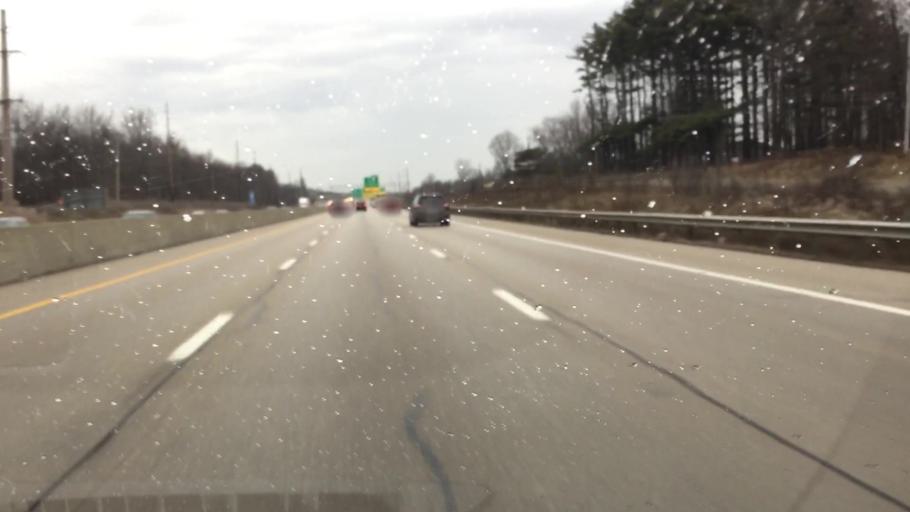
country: US
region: Ohio
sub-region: Summit County
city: Boston Heights
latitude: 41.2434
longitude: -81.4960
